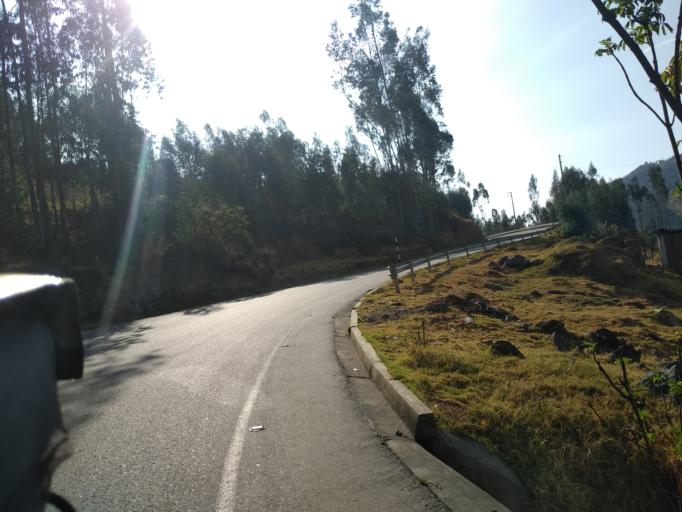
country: PE
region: La Libertad
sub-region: Provincia de Otuzco
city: Agallpampa
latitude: -7.9956
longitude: -78.5139
